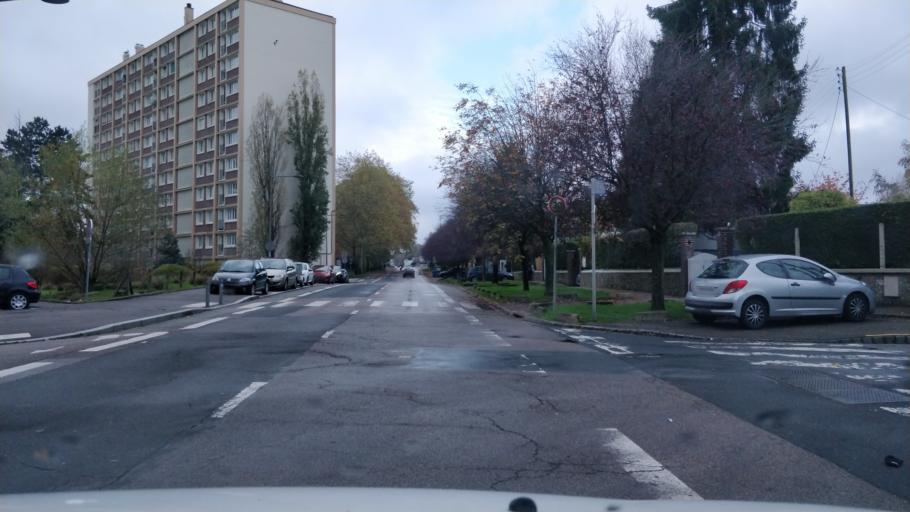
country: FR
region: Haute-Normandie
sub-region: Departement de la Seine-Maritime
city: Bois-Guillaume
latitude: 49.4577
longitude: 1.1275
